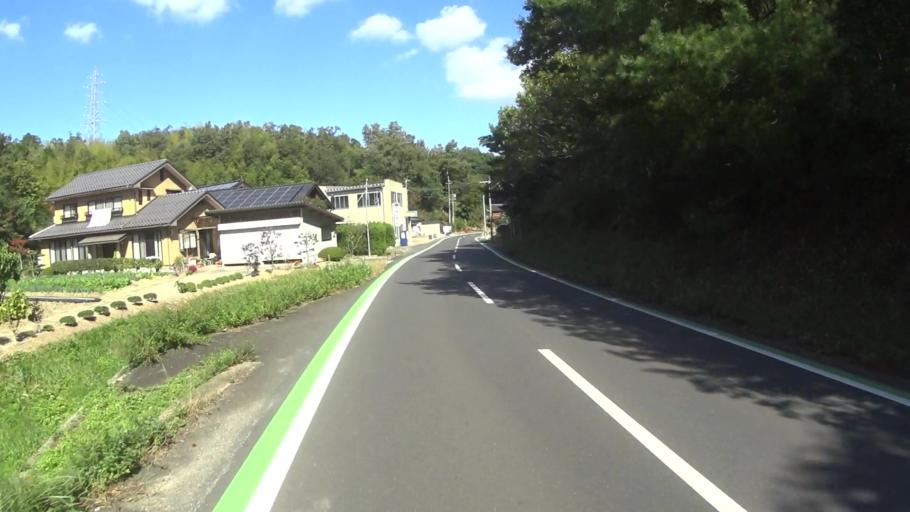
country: JP
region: Kyoto
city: Miyazu
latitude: 35.6382
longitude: 135.0702
